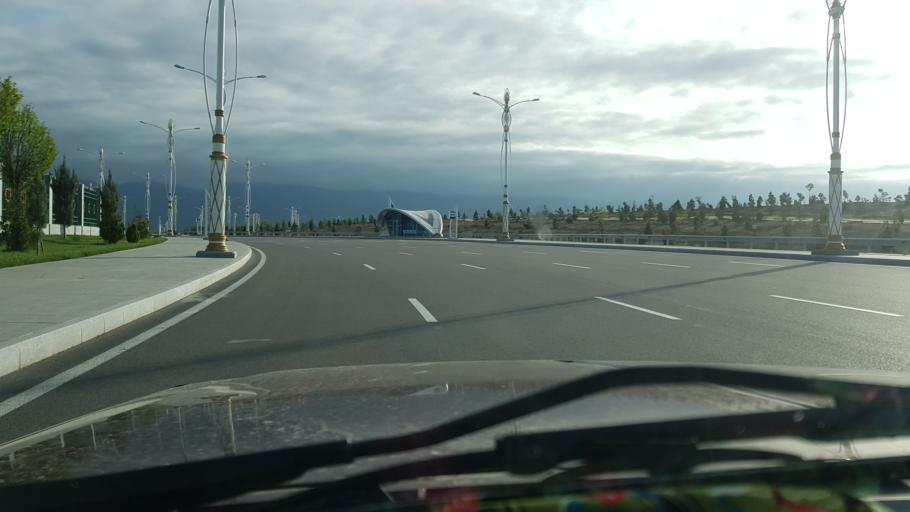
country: TM
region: Ahal
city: Ashgabat
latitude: 37.9308
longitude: 58.3323
